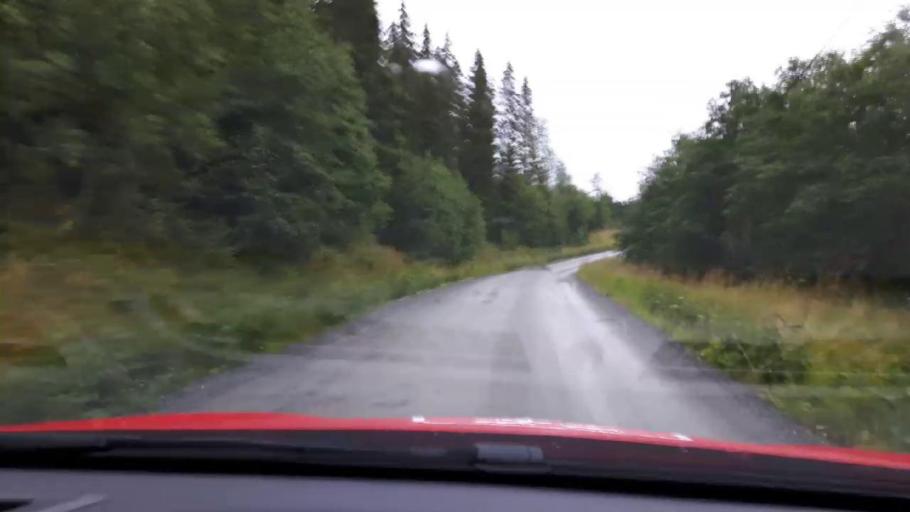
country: SE
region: Jaemtland
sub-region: Are Kommun
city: Are
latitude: 63.5004
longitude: 12.7570
